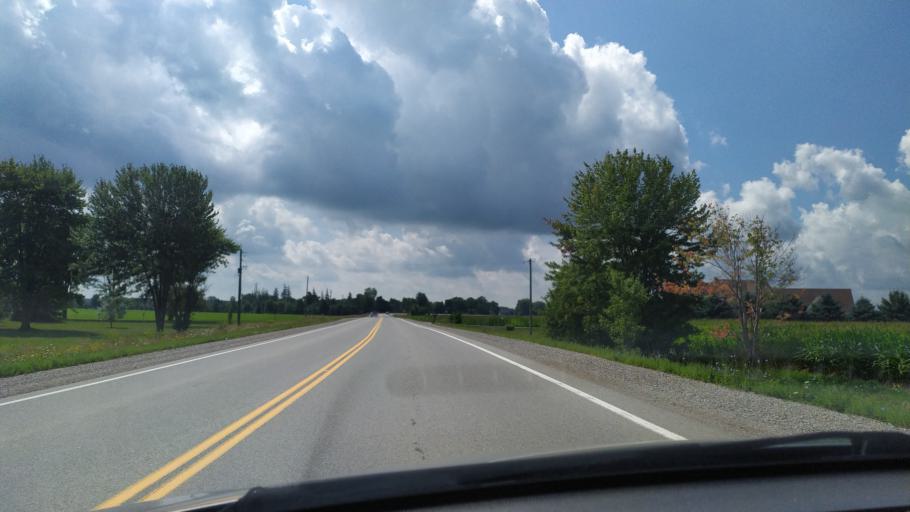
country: CA
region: Ontario
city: Huron East
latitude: 43.3930
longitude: -81.2602
